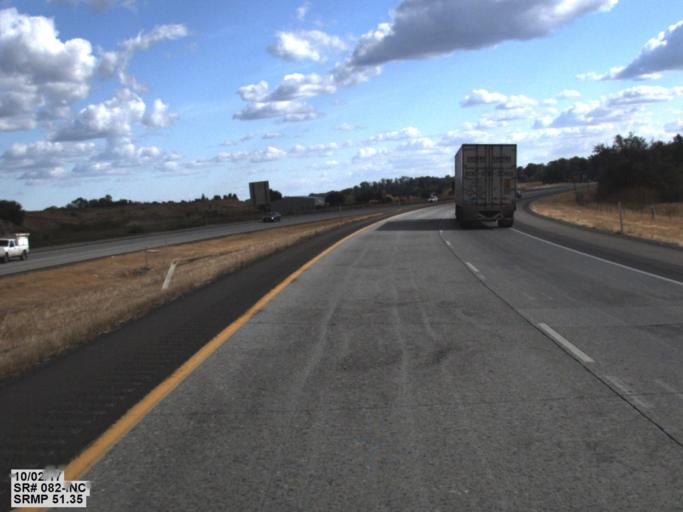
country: US
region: Washington
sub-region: Yakima County
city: Zillah
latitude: 46.4103
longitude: -120.2895
